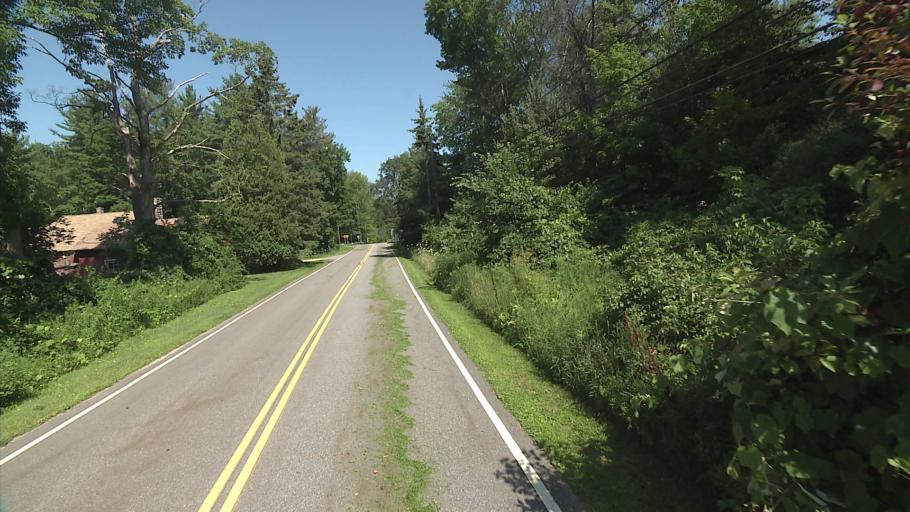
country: US
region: Connecticut
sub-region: Litchfield County
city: Winchester Center
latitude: 41.9027
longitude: -73.1415
